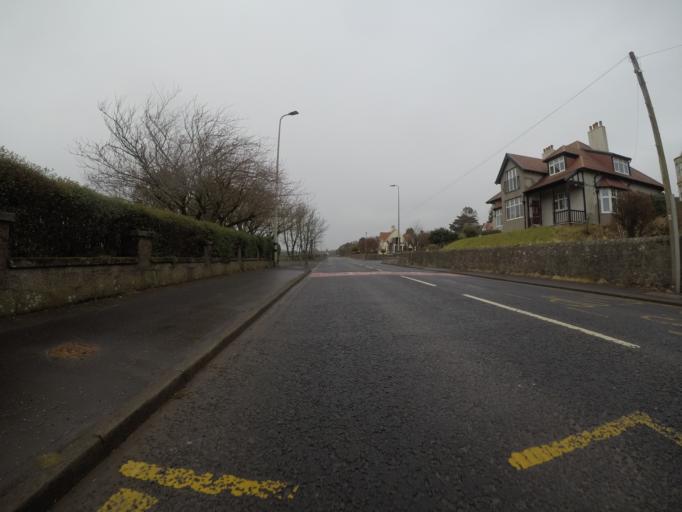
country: GB
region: Scotland
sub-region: North Ayrshire
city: West Kilbride
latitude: 55.6919
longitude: -4.8658
